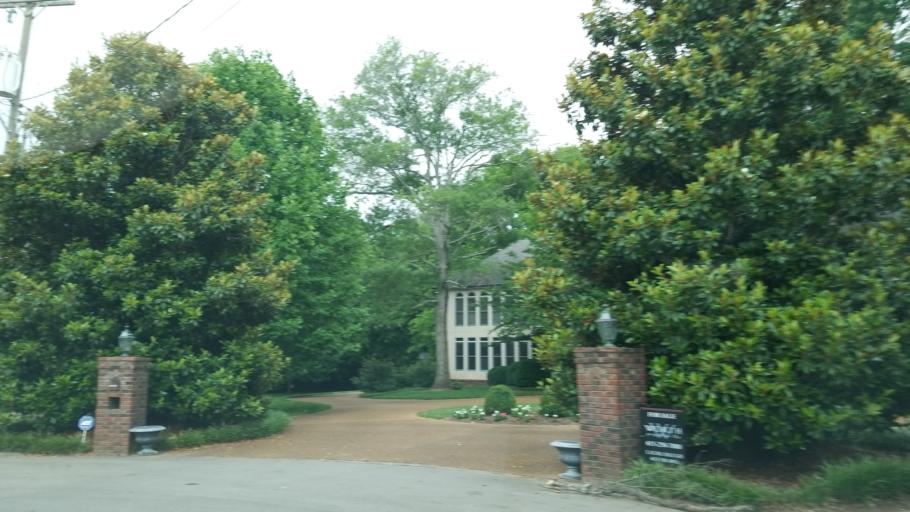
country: US
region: Tennessee
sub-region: Davidson County
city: Forest Hills
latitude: 36.0409
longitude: -86.8397
